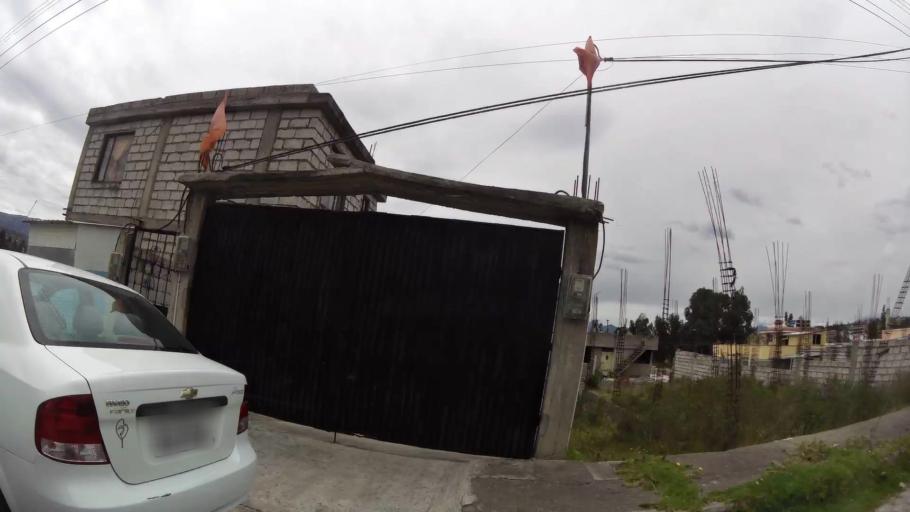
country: EC
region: Cotopaxi
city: Latacunga
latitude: -0.9526
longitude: -78.6048
